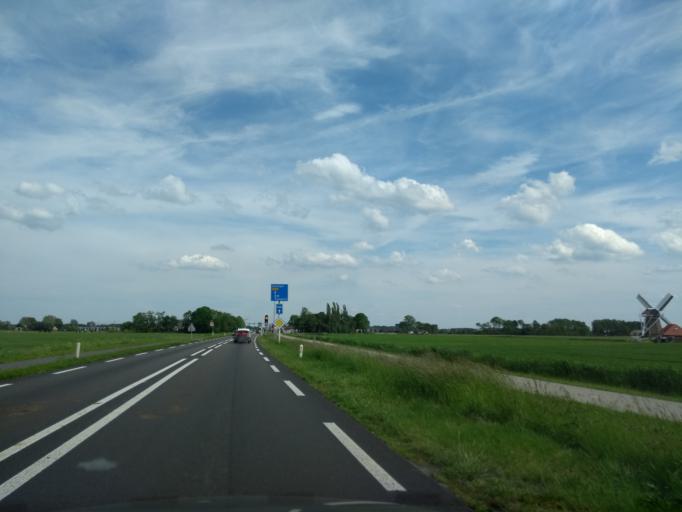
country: NL
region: Groningen
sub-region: Gemeente Zuidhorn
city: Aduard
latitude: 53.2440
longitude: 6.4894
